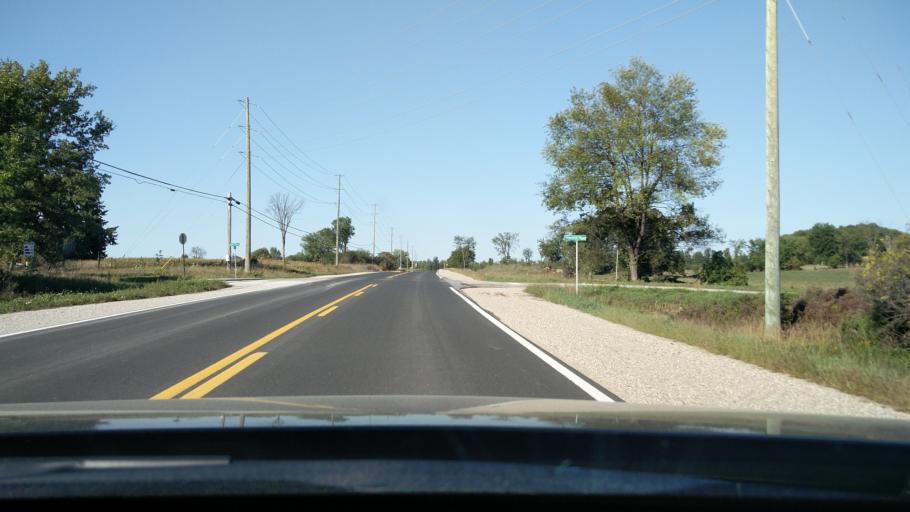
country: CA
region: Ontario
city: Perth
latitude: 44.8327
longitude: -76.3119
